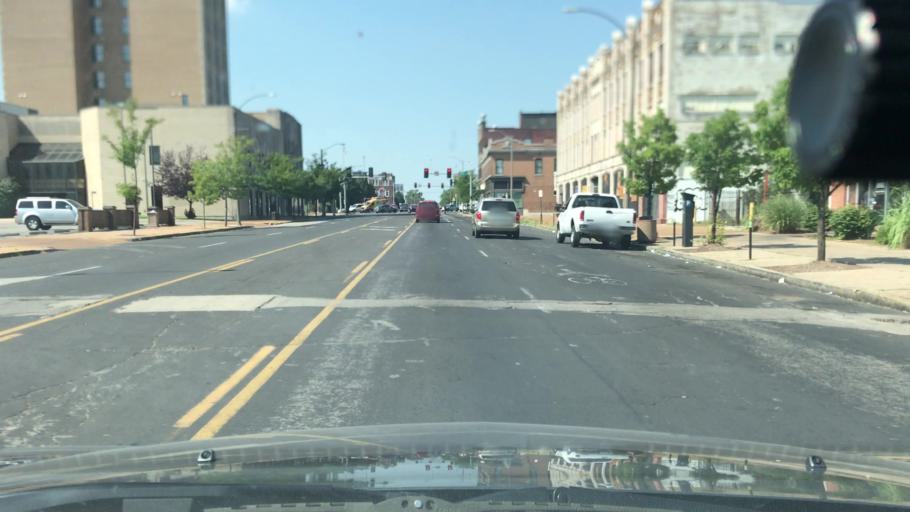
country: US
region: Illinois
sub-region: Saint Clair County
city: Cahokia
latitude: 38.5910
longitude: -90.2440
